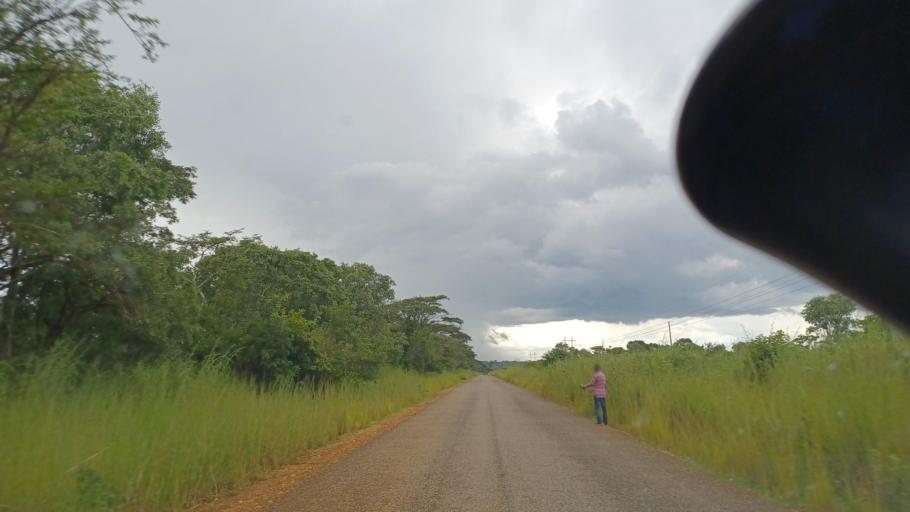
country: ZM
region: North-Western
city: Kasempa
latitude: -13.0050
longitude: 26.0109
